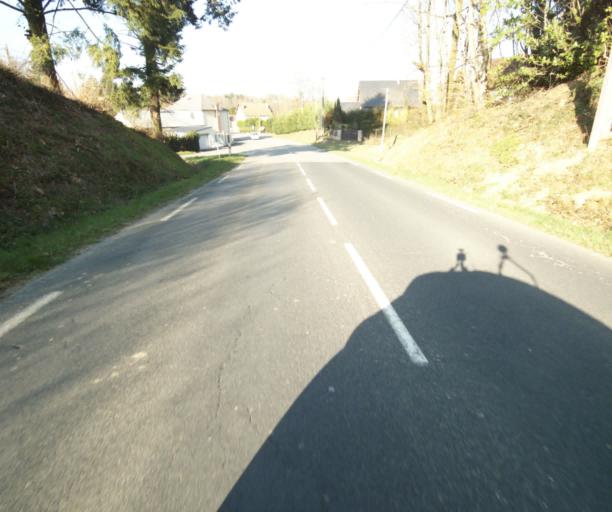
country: FR
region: Limousin
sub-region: Departement de la Correze
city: Saint-Clement
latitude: 45.3229
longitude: 1.6791
